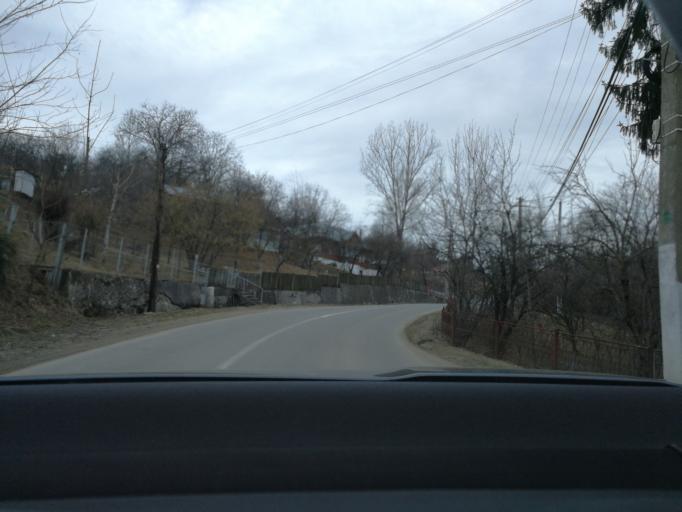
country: RO
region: Prahova
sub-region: Comuna Telega
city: Telega
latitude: 45.1407
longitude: 25.7838
